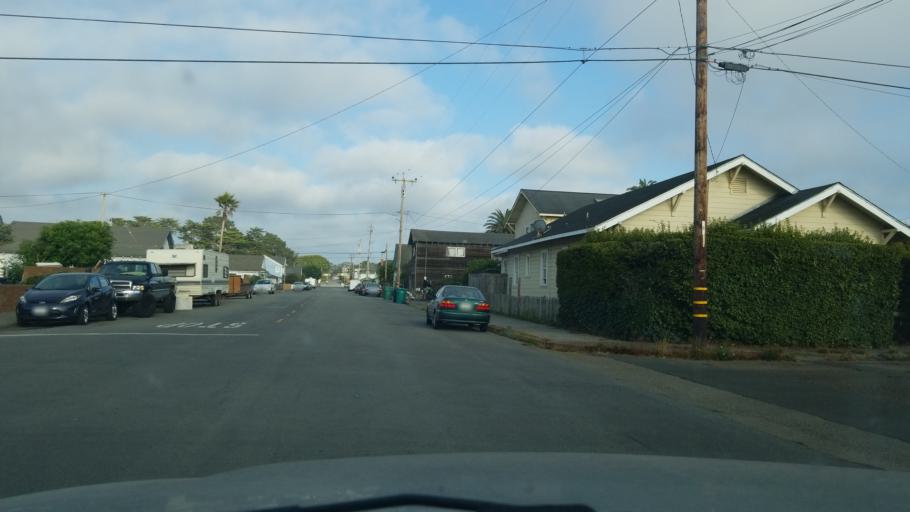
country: US
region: California
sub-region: Mendocino County
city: Fort Bragg
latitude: 39.4493
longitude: -123.8087
